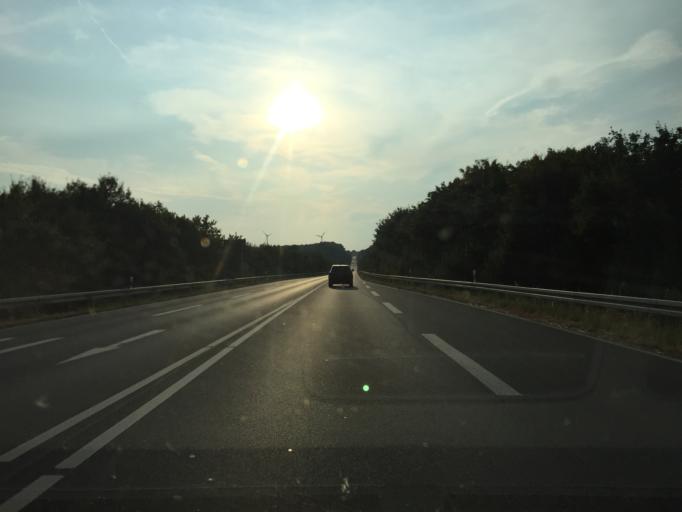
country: DE
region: Lower Saxony
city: Marklohe
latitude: 52.6536
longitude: 9.1476
